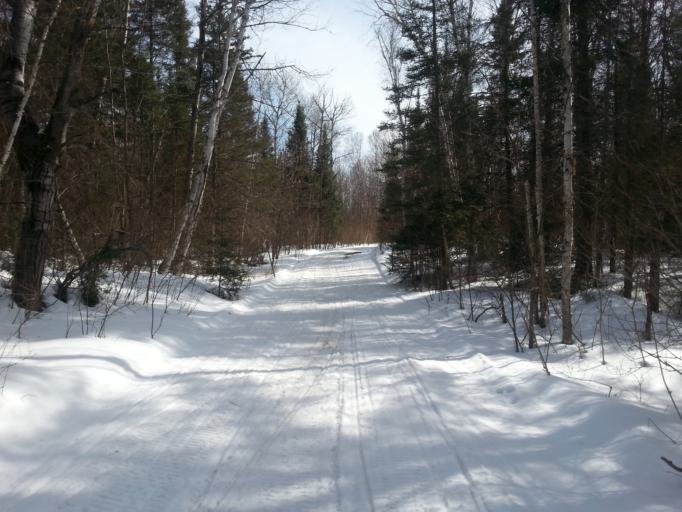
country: CA
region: Ontario
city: Greater Sudbury
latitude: 46.3475
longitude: -80.9014
